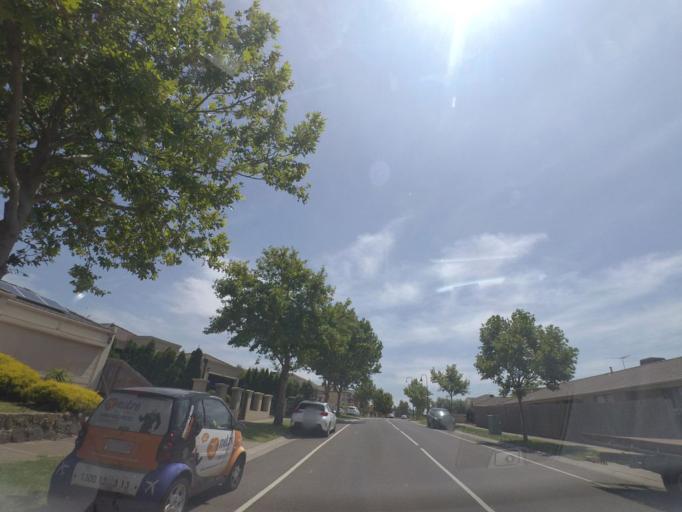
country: AU
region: Victoria
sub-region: Hume
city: Roxburgh Park
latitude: -37.6188
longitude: 144.9236
